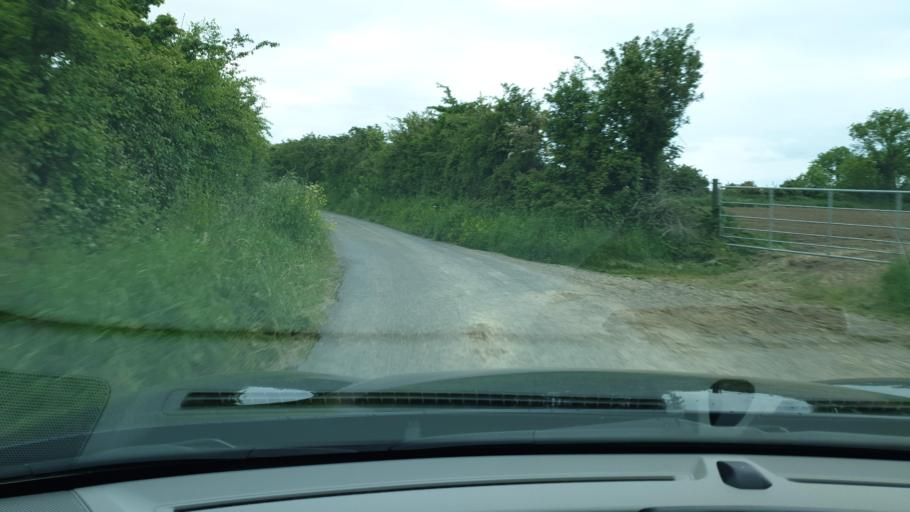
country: IE
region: Leinster
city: Balrothery
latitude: 53.5604
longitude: -6.1966
